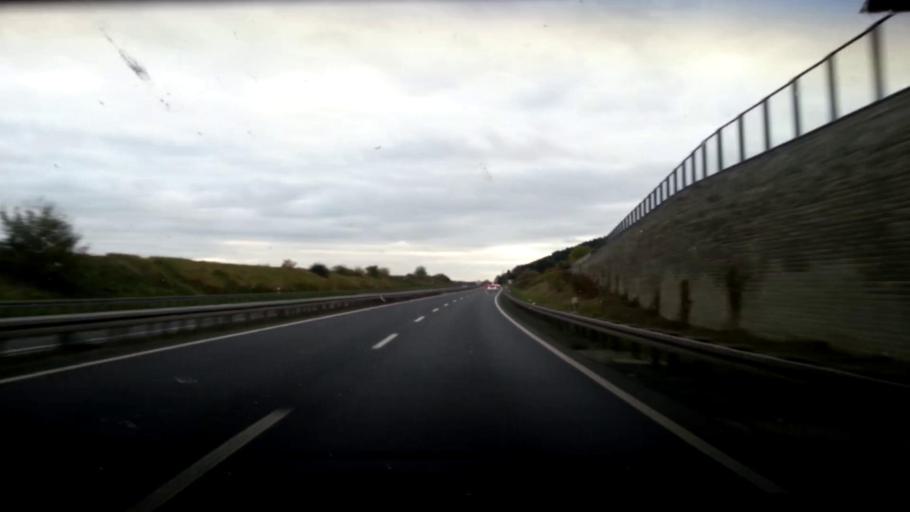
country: DE
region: Bavaria
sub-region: Upper Franconia
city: Kronach
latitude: 50.2208
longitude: 11.3103
